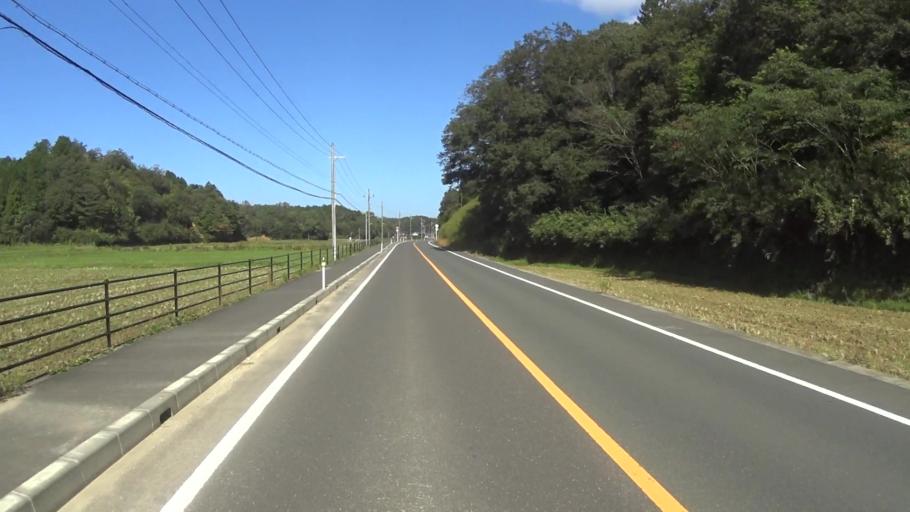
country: JP
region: Kyoto
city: Miyazu
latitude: 35.6472
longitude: 135.0695
